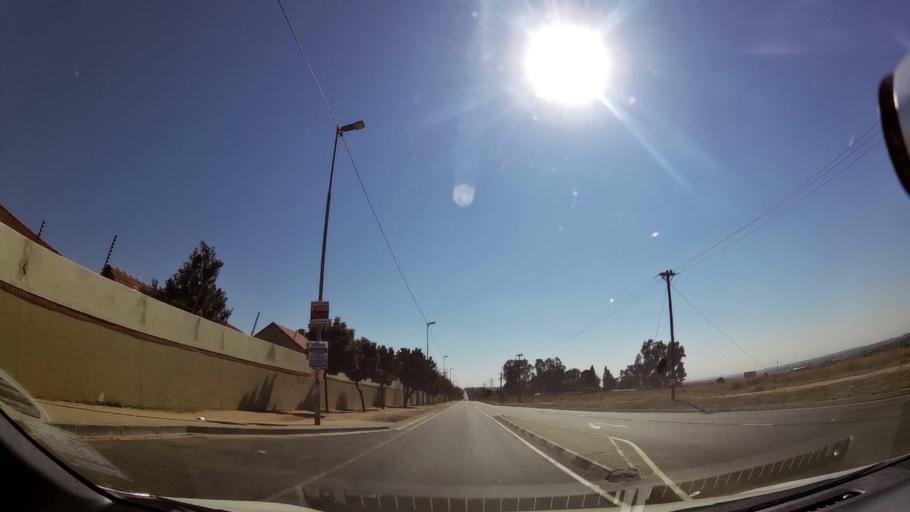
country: ZA
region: Gauteng
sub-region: City of Johannesburg Metropolitan Municipality
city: Midrand
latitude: -25.9647
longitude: 28.1016
